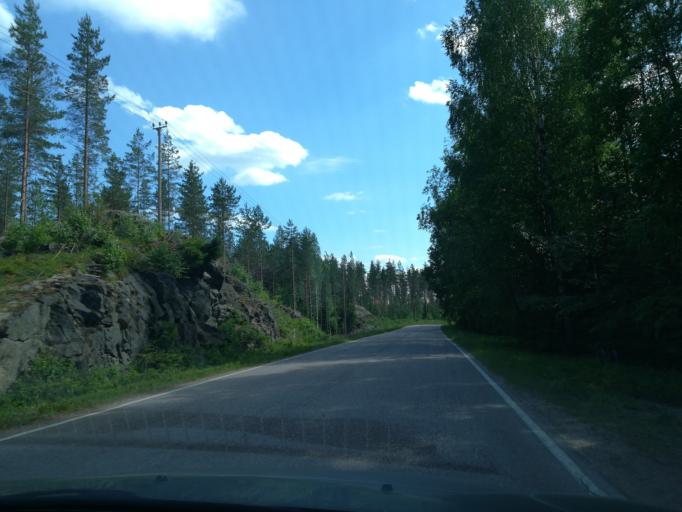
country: FI
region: South Karelia
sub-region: Imatra
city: Ruokolahti
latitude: 61.4811
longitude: 28.7880
